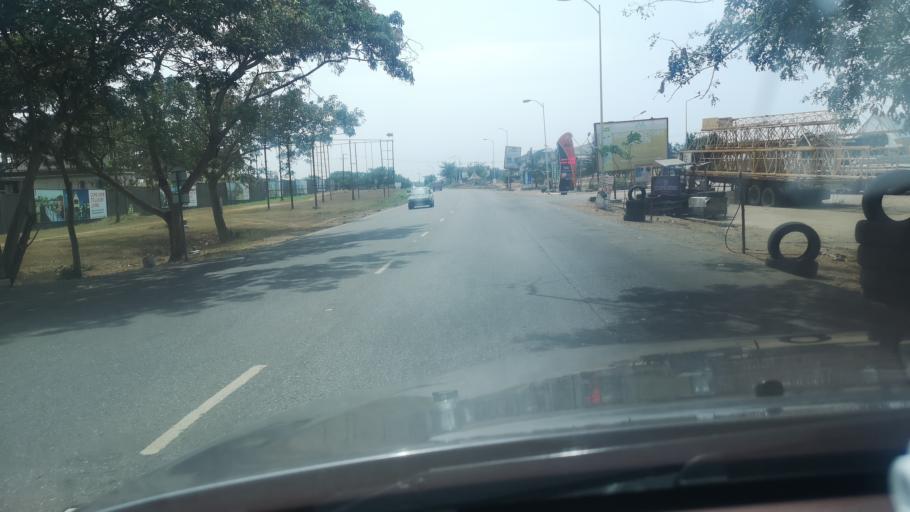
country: GH
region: Greater Accra
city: Nungua
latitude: 5.6157
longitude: -0.0614
